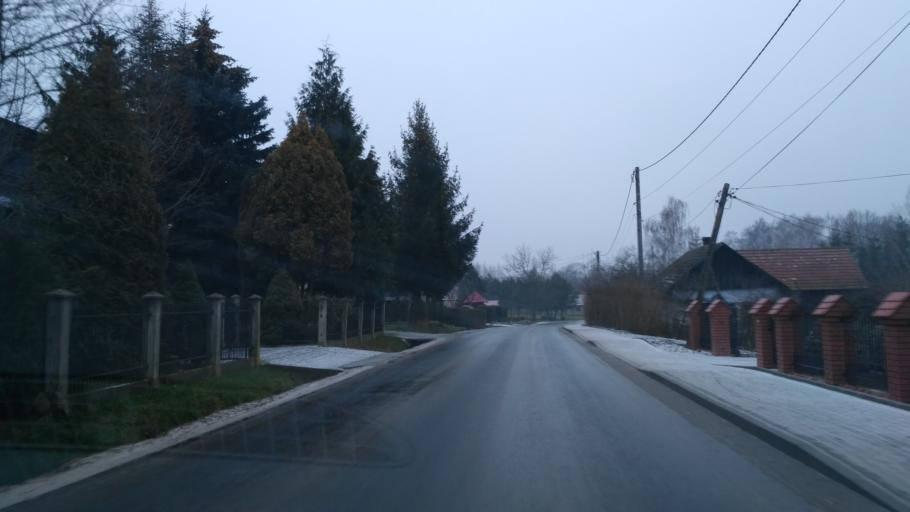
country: PL
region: Subcarpathian Voivodeship
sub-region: Powiat przeworski
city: Kanczuga
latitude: 50.0176
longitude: 22.4010
